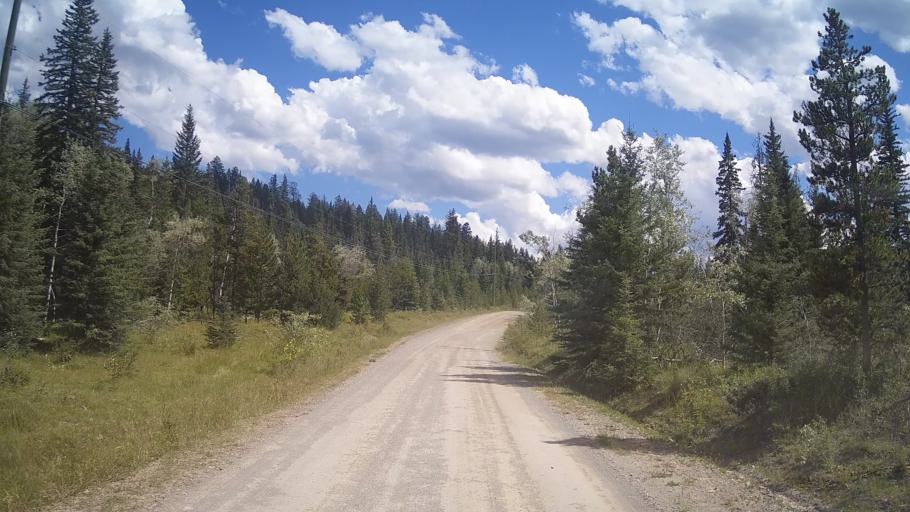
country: CA
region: British Columbia
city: Lillooet
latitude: 51.2921
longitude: -121.9782
